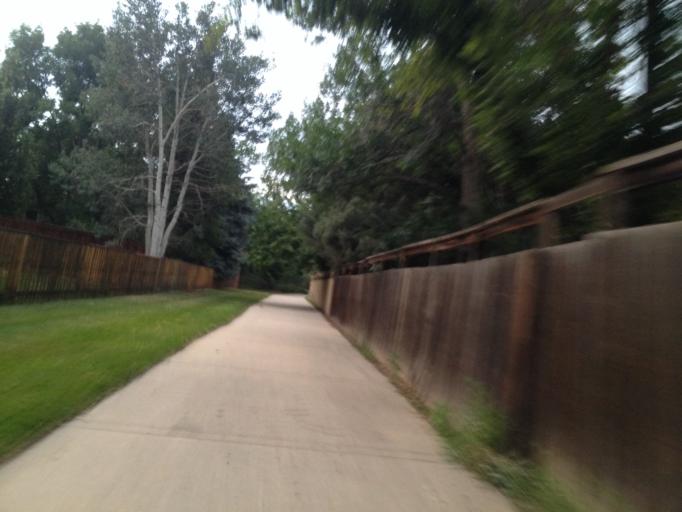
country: US
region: Colorado
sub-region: Boulder County
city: Superior
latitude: 39.9643
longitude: -105.1539
